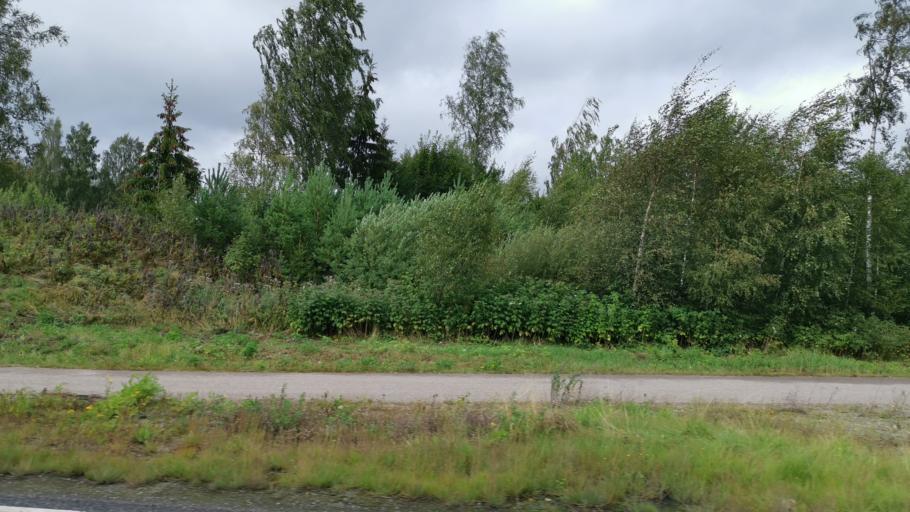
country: SE
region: Vaestra Goetaland
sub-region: Trollhattan
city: Trollhattan
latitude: 58.3337
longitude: 12.2300
